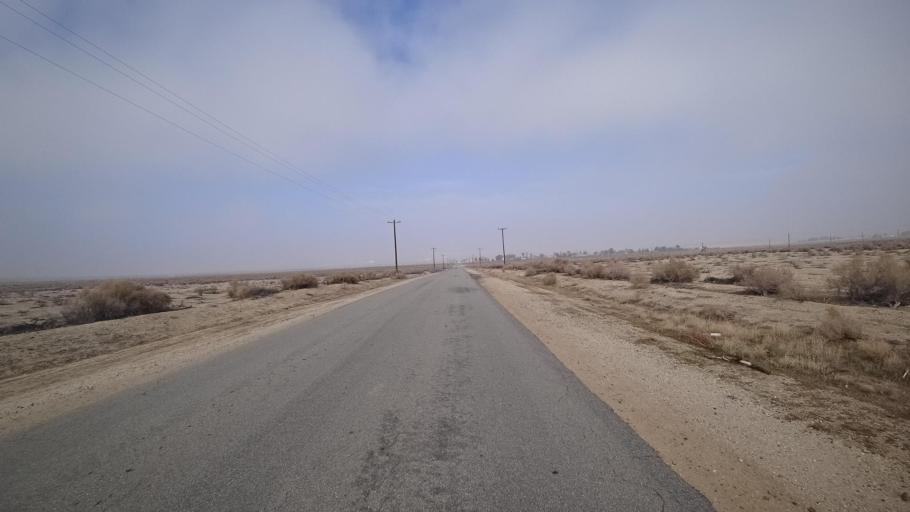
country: US
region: California
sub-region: Kern County
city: Ford City
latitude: 35.2008
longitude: -119.4290
